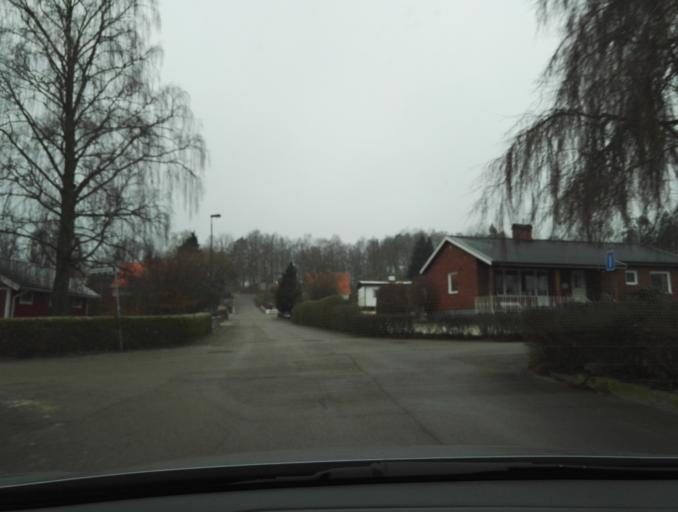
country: SE
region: Kronoberg
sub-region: Vaxjo Kommun
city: Vaexjoe
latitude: 56.9006
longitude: 14.7373
